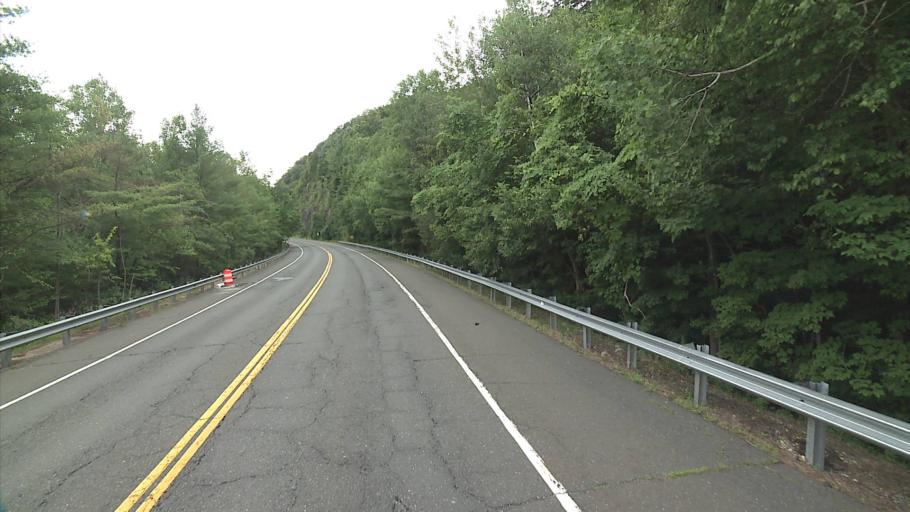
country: US
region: Connecticut
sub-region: Litchfield County
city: Winsted
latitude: 42.0176
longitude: -73.0527
